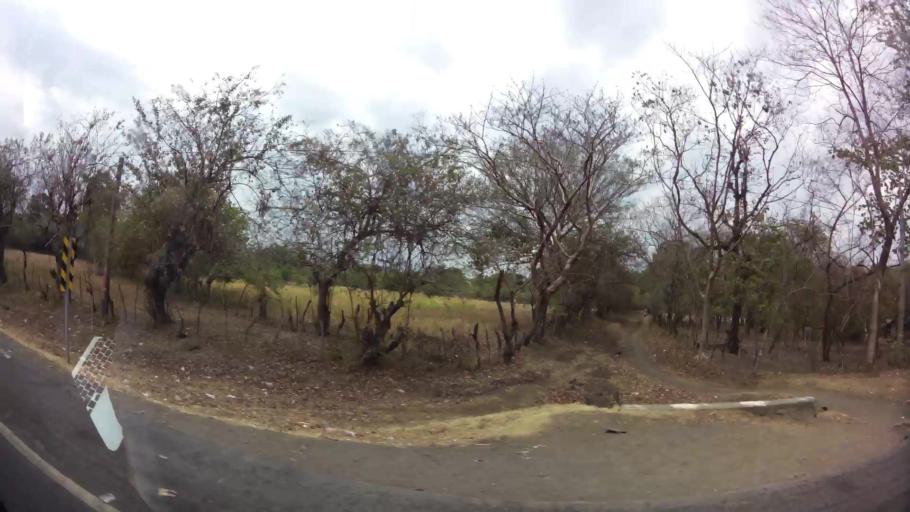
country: NI
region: Leon
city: Telica
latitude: 12.5199
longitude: -86.8671
